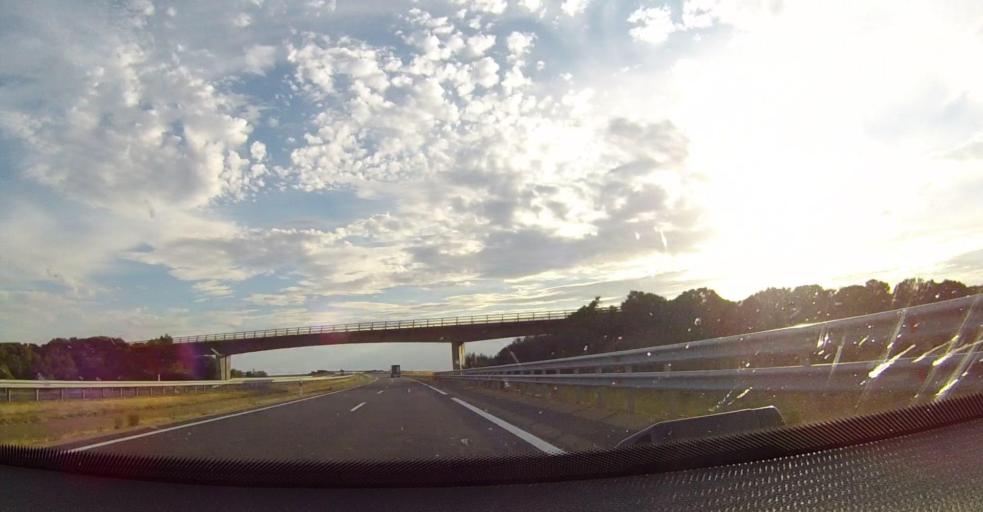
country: ES
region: Castille and Leon
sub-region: Provincia de Palencia
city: Villasarracino
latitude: 42.3830
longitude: -4.4990
